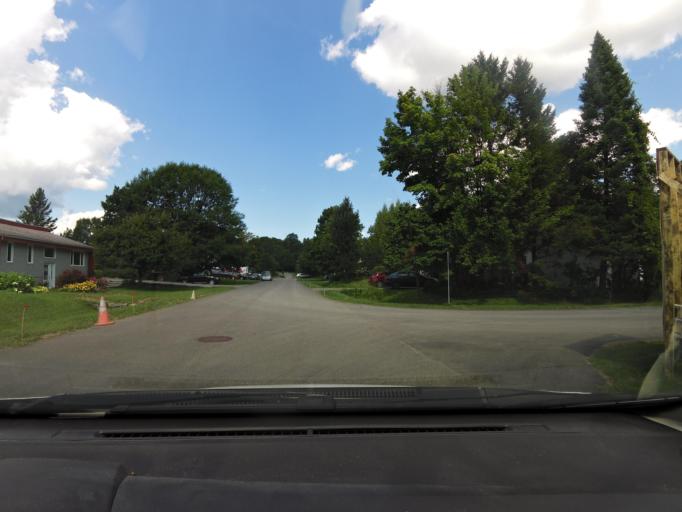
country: CA
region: Quebec
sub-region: Capitale-Nationale
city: Neuville
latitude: 46.7159
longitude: -71.5428
